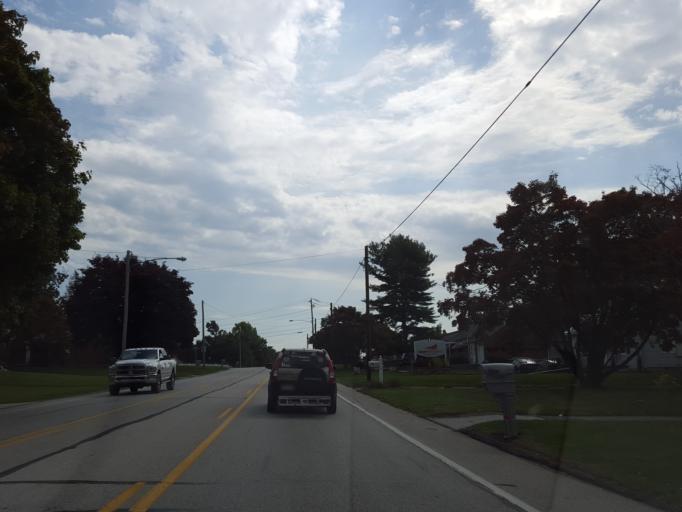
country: US
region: Pennsylvania
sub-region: York County
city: Spry
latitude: 39.9291
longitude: -76.6870
